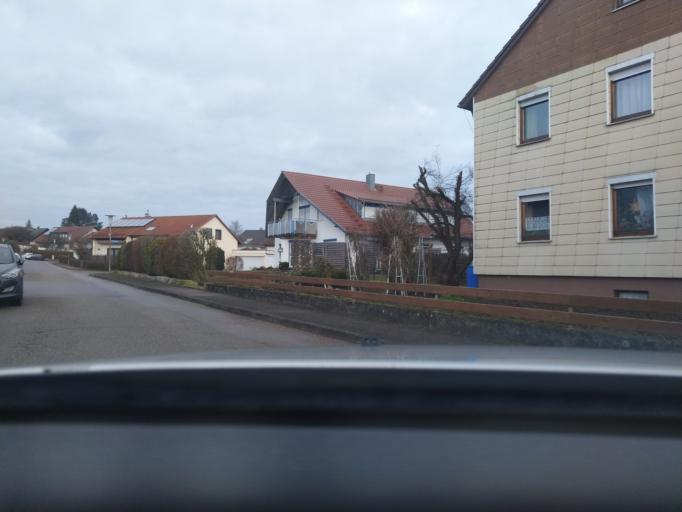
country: DE
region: Baden-Wuerttemberg
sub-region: Regierungsbezirk Stuttgart
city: Durlangen
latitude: 48.8601
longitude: 9.7940
